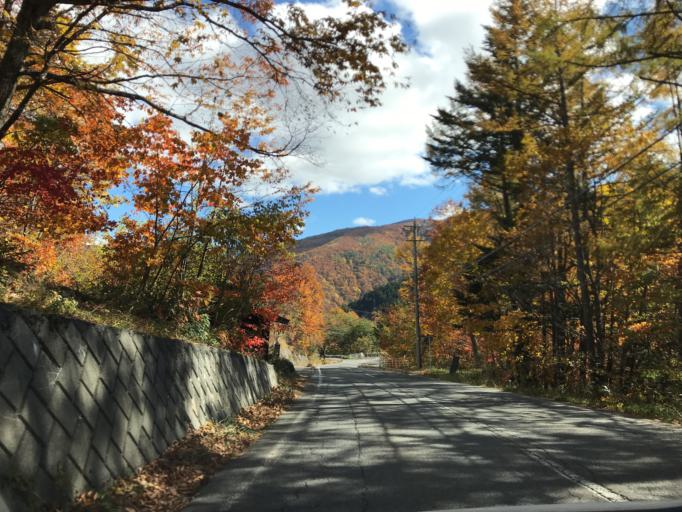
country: JP
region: Nagano
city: Toyoshina
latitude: 36.1253
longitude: 137.6503
